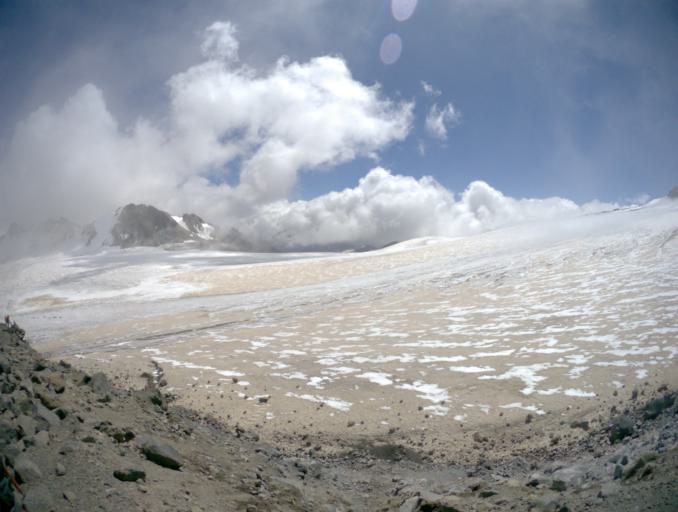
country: RU
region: Kabardino-Balkariya
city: Terskol
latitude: 43.3440
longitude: 42.5081
